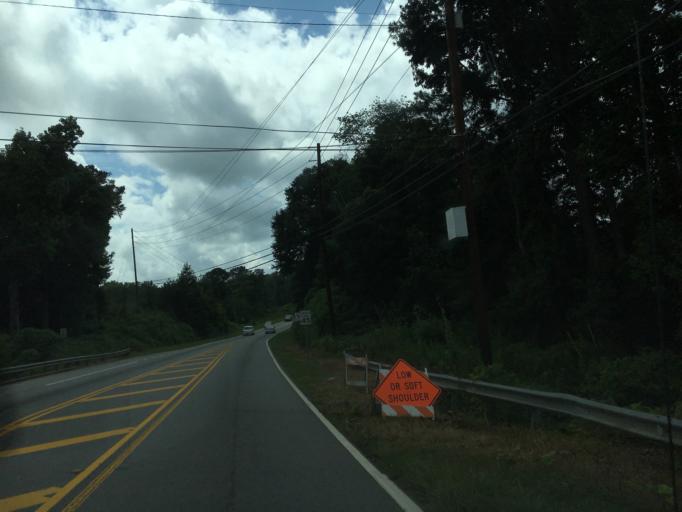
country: US
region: Georgia
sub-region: Rockdale County
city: Lakeview Estates
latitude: 33.6866
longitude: -84.0330
